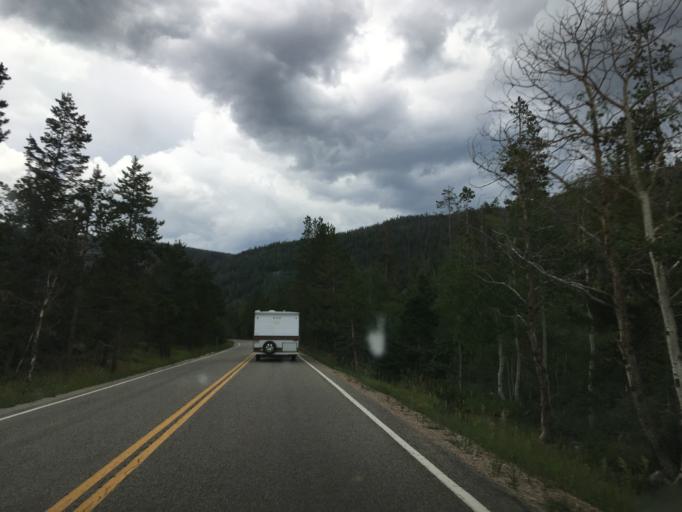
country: US
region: Utah
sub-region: Summit County
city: Francis
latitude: 40.5933
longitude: -110.9805
